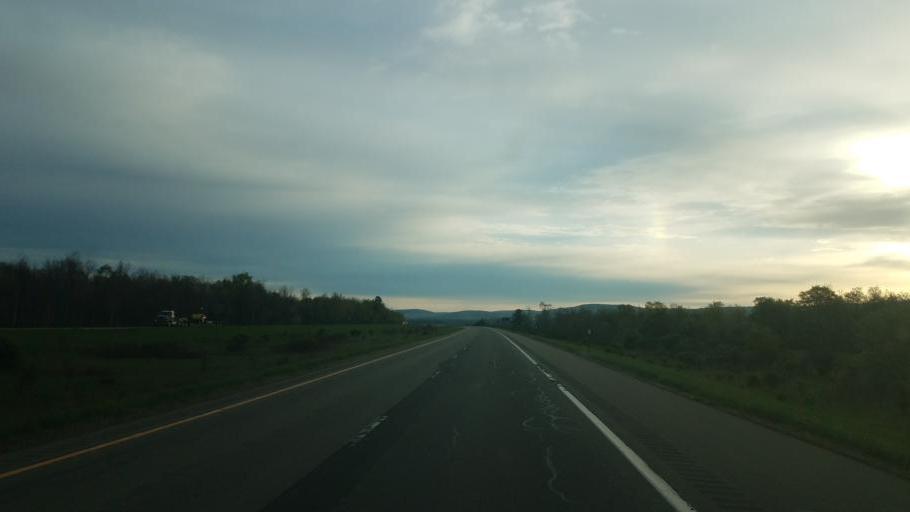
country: US
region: New York
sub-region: Allegany County
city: Belmont
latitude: 42.2493
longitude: -78.0733
